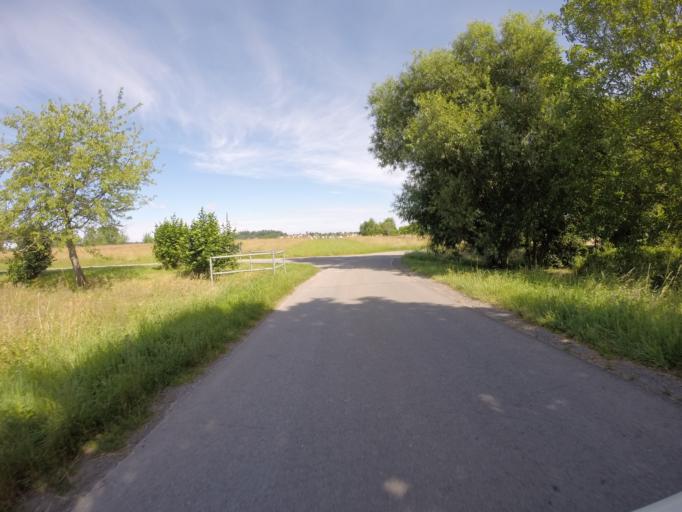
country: DE
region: Baden-Wuerttemberg
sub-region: Karlsruhe Region
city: Dobel
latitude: 48.8573
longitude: 8.5118
